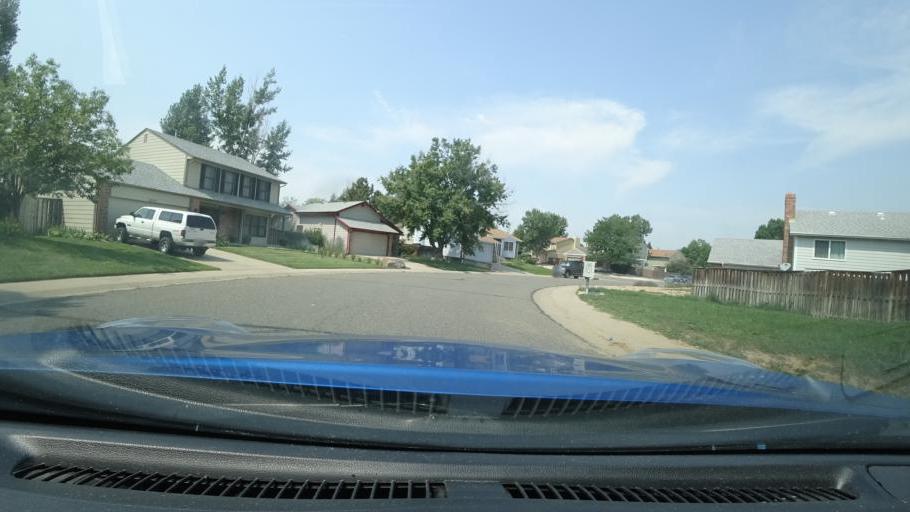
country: US
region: Colorado
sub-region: Adams County
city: Aurora
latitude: 39.7800
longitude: -104.7640
